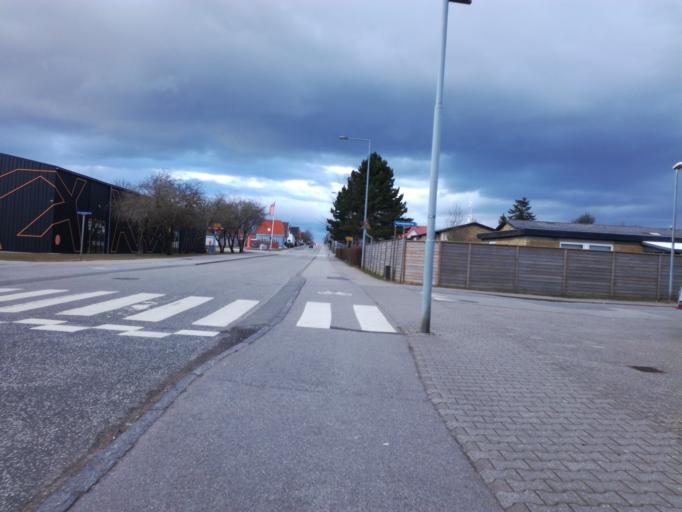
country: DK
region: South Denmark
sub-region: Fredericia Kommune
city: Fredericia
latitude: 55.5773
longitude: 9.7669
